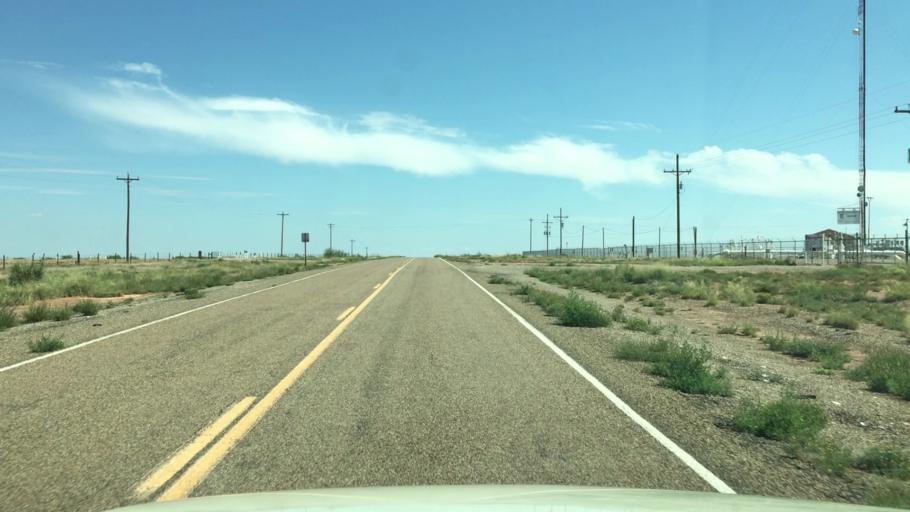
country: US
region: New Mexico
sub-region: Chaves County
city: Roswell
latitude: 33.9639
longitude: -104.5823
